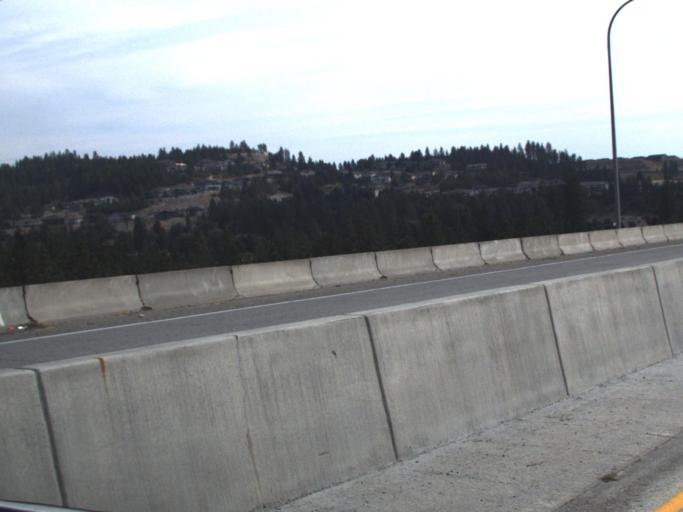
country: US
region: Washington
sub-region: Spokane County
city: Fairwood
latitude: 47.7865
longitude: -117.4069
